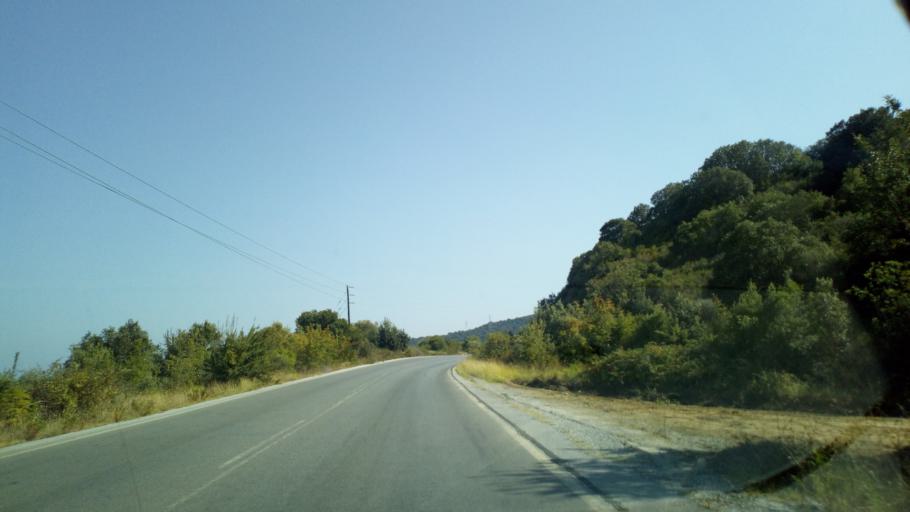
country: GR
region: Central Macedonia
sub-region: Nomos Thessalonikis
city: Stavros
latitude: 40.6447
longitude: 23.7469
